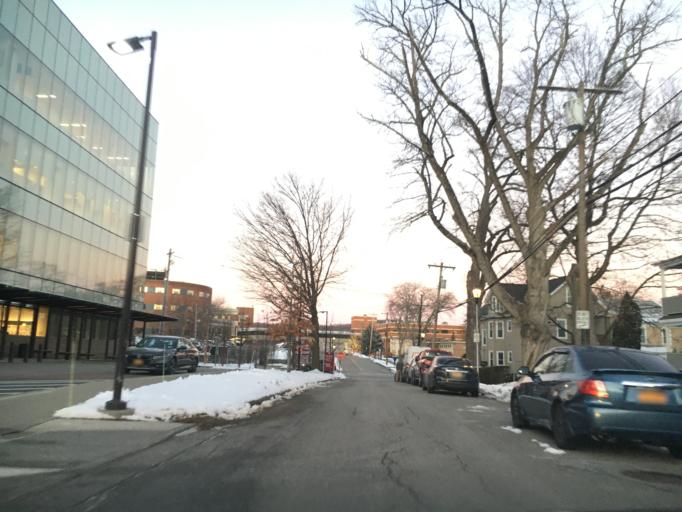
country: US
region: New York
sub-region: Dutchess County
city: Poughkeepsie
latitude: 41.6942
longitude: -73.9331
